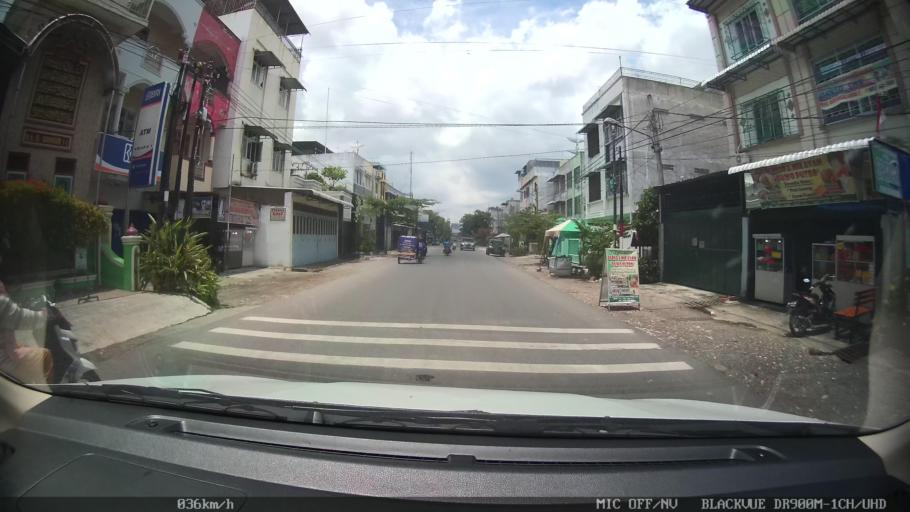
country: ID
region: North Sumatra
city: Medan
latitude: 3.5946
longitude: 98.7094
